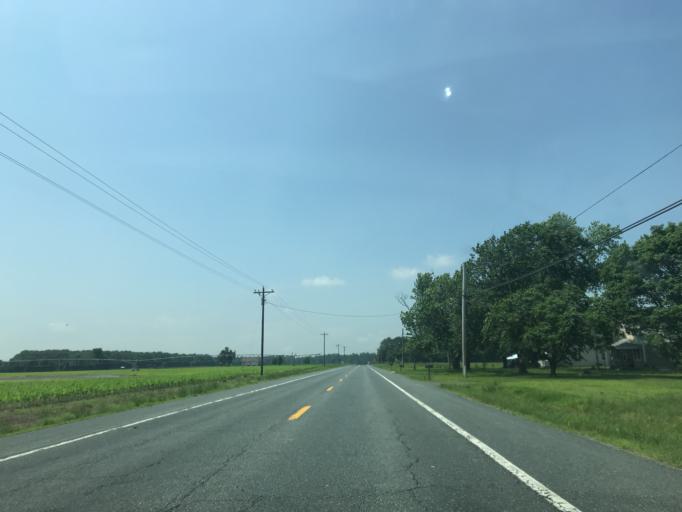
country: US
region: Maryland
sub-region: Caroline County
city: Federalsburg
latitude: 38.6537
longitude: -75.7246
